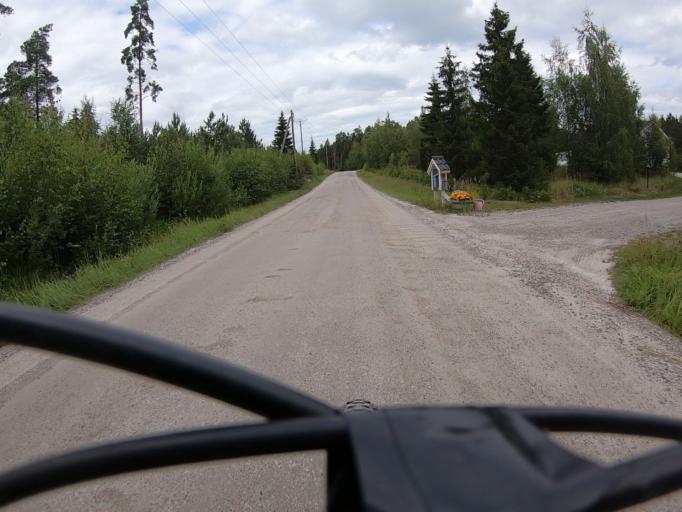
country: FI
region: Varsinais-Suomi
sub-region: Vakka-Suomi
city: Uusikaupunki
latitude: 60.8411
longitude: 21.3851
